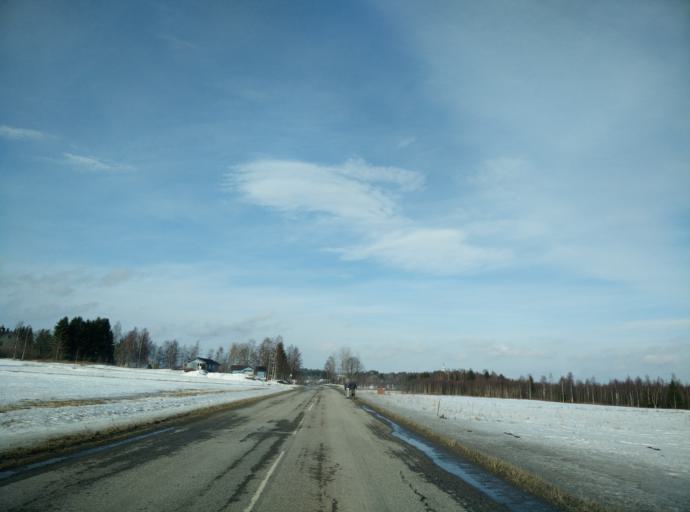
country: SE
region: Vaesternorrland
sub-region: Sundsvalls Kommun
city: Njurundabommen
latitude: 62.2422
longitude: 17.3797
